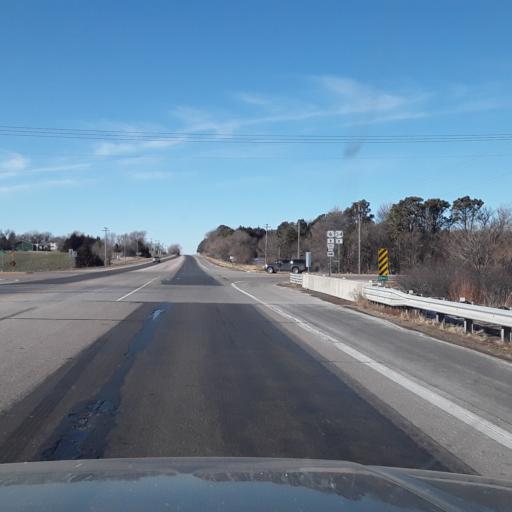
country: US
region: Nebraska
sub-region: Adams County
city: Hastings
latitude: 40.5681
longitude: -98.4388
